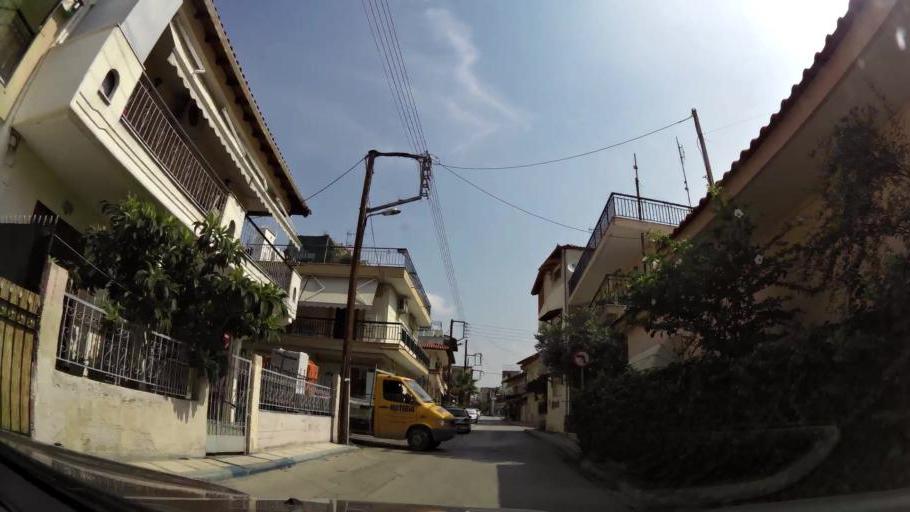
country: GR
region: Central Macedonia
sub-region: Nomos Thessalonikis
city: Stavroupoli
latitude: 40.6712
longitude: 22.9354
